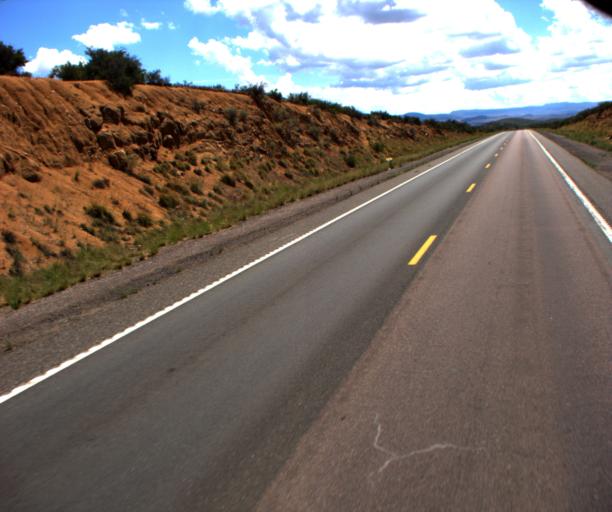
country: US
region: Arizona
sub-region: Yavapai County
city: Dewey-Humboldt
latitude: 34.5430
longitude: -112.1538
